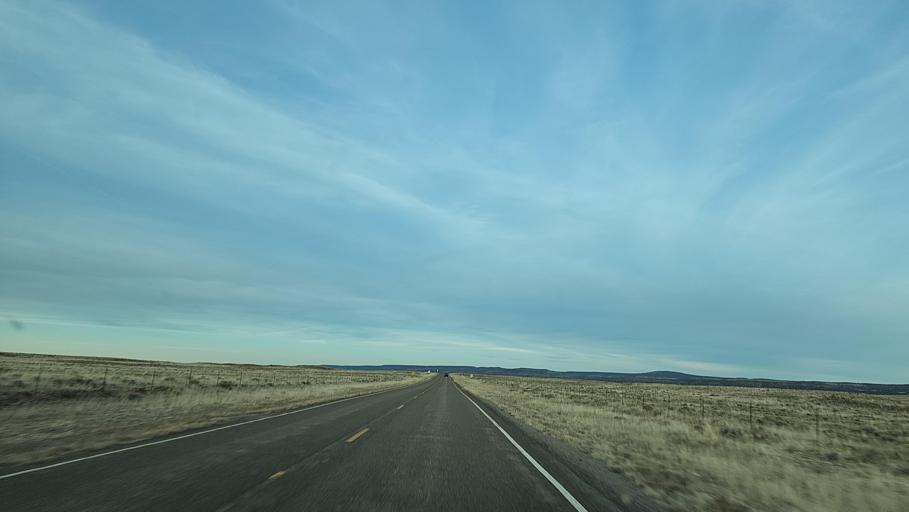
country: US
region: New Mexico
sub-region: Cibola County
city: Grants
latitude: 34.6854
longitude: -108.0673
